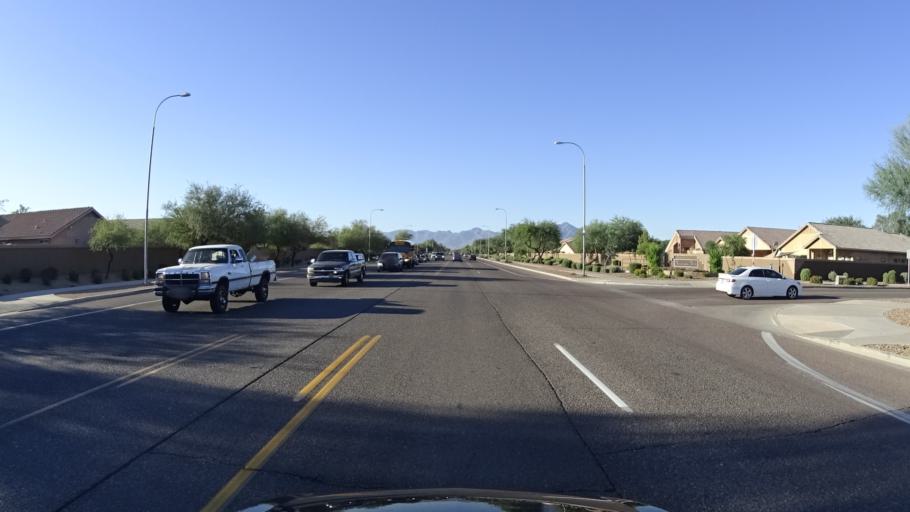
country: US
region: Arizona
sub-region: Maricopa County
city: Tolleson
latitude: 33.4336
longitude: -112.2384
